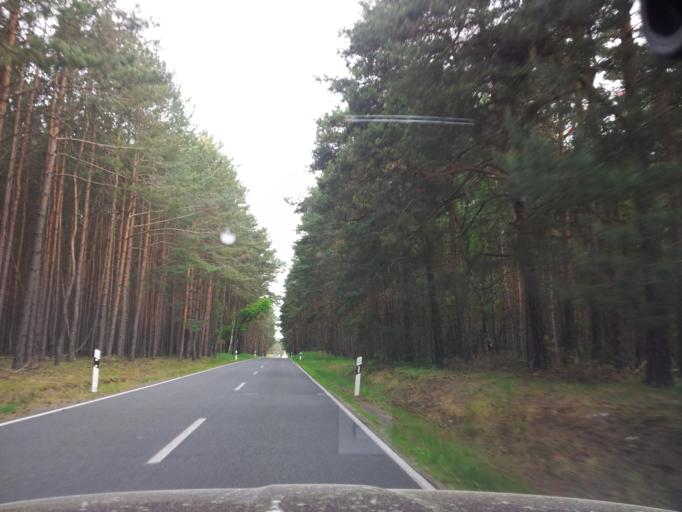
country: DE
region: Brandenburg
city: Linthe
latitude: 52.0838
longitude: 12.8011
